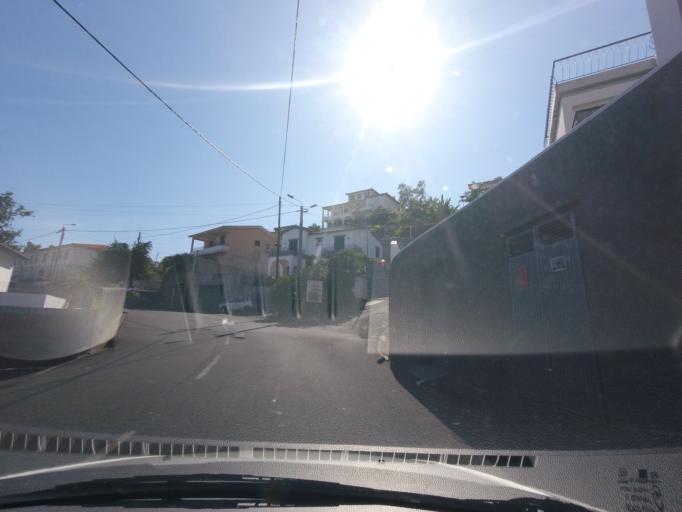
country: PT
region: Madeira
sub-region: Funchal
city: Nossa Senhora do Monte
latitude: 32.6668
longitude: -16.9121
